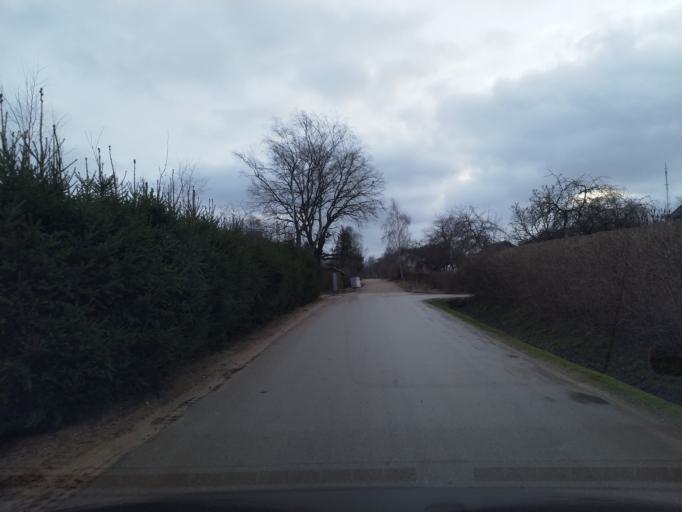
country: LV
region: Kuldigas Rajons
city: Kuldiga
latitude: 56.9457
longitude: 22.0072
